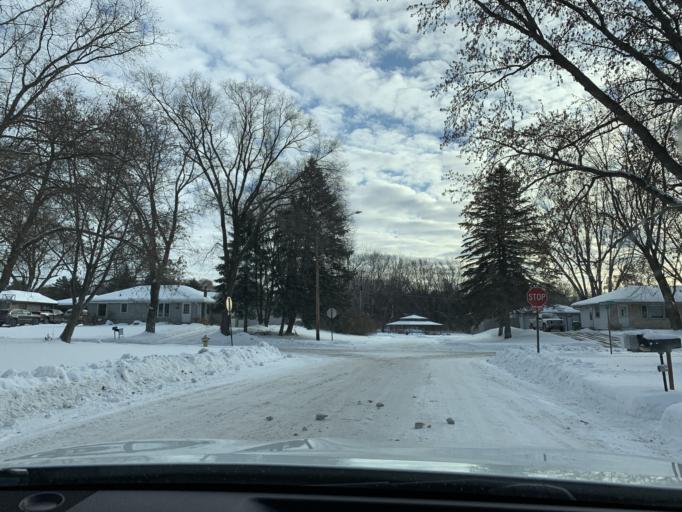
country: US
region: Minnesota
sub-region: Anoka County
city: Coon Rapids
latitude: 45.1717
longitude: -93.2856
